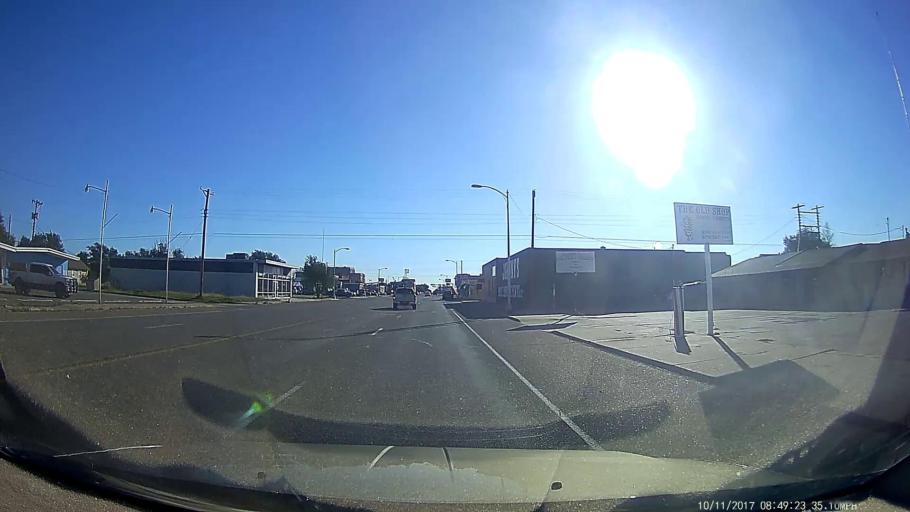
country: US
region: New Mexico
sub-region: Curry County
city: Clovis
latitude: 34.4047
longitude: -103.2086
